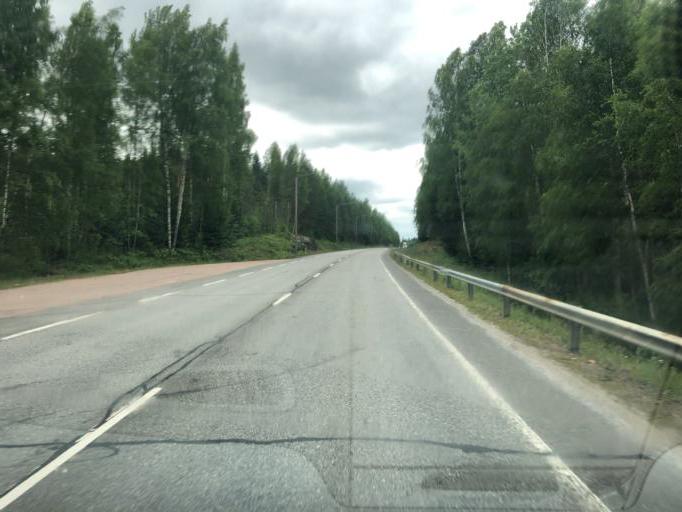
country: FI
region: Kymenlaakso
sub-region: Kouvola
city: Kouvola
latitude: 60.8987
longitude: 26.7460
